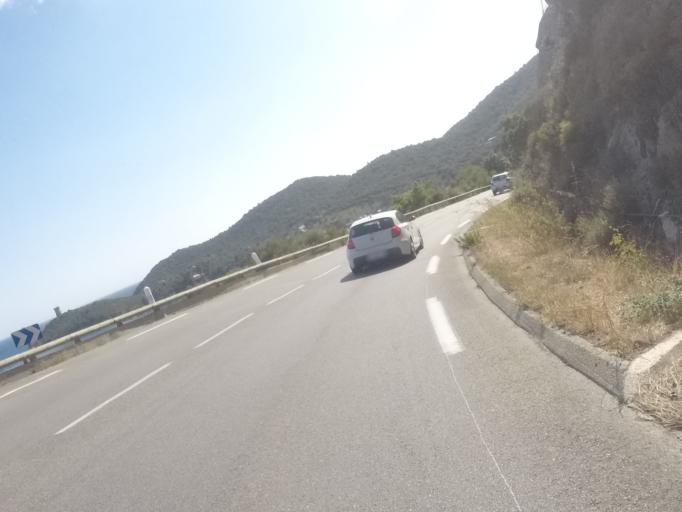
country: FR
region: Corsica
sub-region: Departement de la Corse-du-Sud
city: Sari-Solenzara
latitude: 41.7214
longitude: 9.4047
